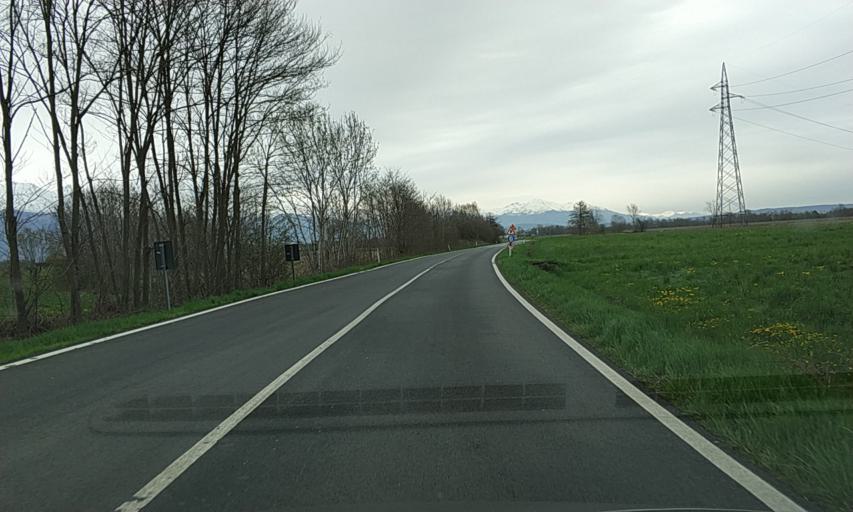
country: IT
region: Piedmont
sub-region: Provincia di Torino
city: Front
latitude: 45.3008
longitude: 7.6757
